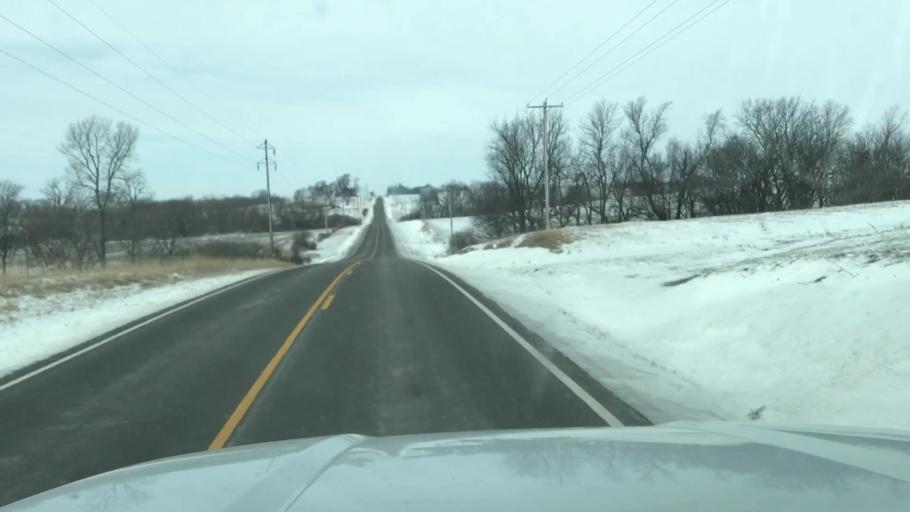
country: US
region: Missouri
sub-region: Holt County
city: Mound City
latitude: 40.1301
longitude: -95.1109
